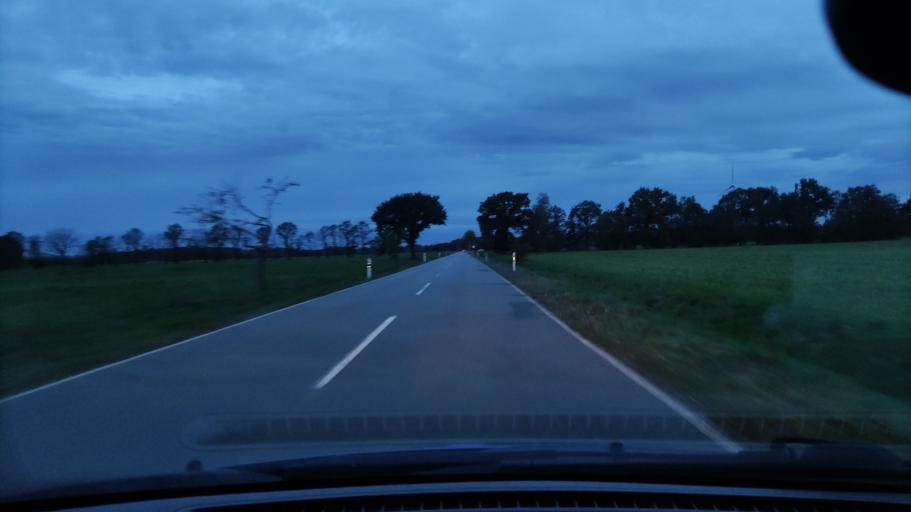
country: DE
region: Lower Saxony
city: Trebel
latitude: 52.9655
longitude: 11.2957
